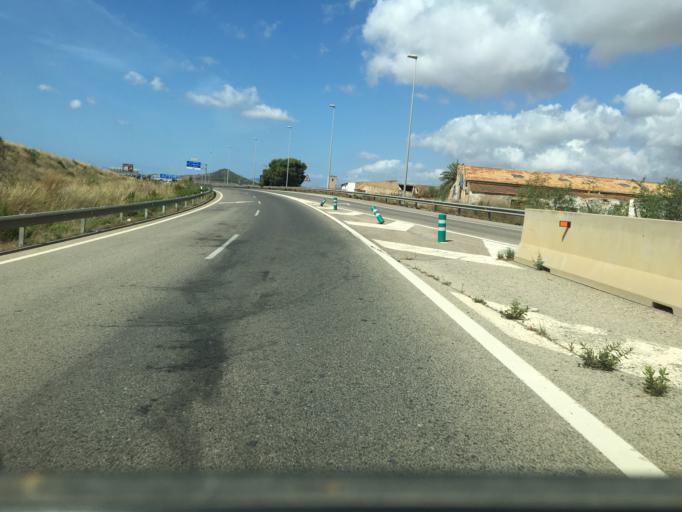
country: ES
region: Murcia
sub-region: Murcia
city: La Union
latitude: 37.6582
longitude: -0.9036
